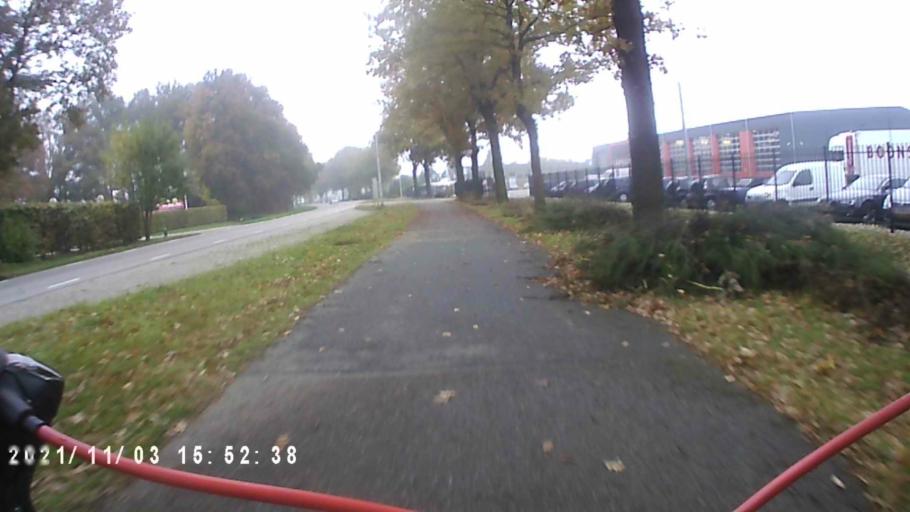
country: NL
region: Groningen
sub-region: Gemeente Leek
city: Leek
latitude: 53.0741
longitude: 6.3318
